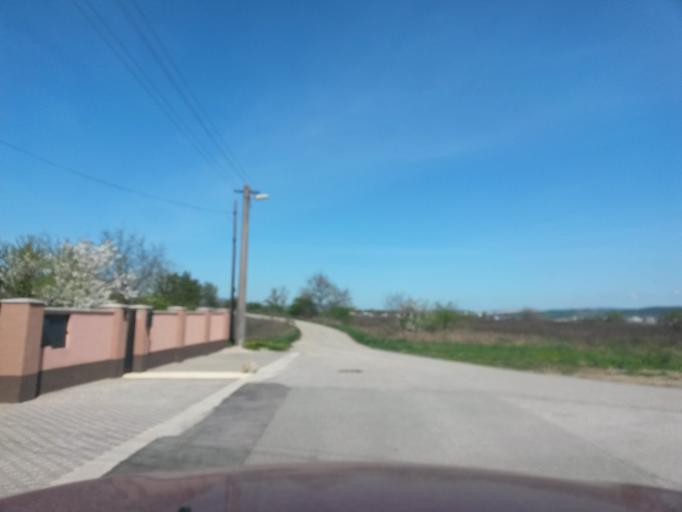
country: SK
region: Kosicky
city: Kosice
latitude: 48.6570
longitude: 21.2639
